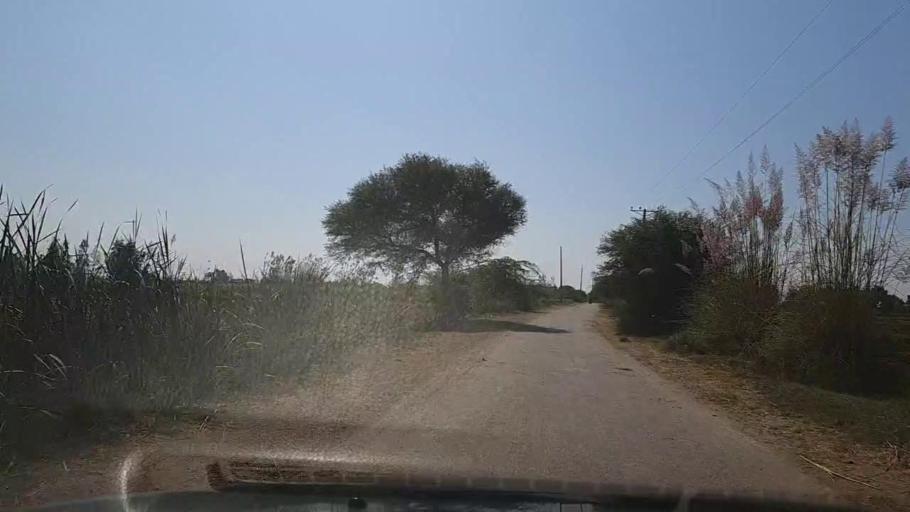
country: PK
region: Sindh
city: Mirpur Sakro
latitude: 24.6029
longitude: 67.7878
